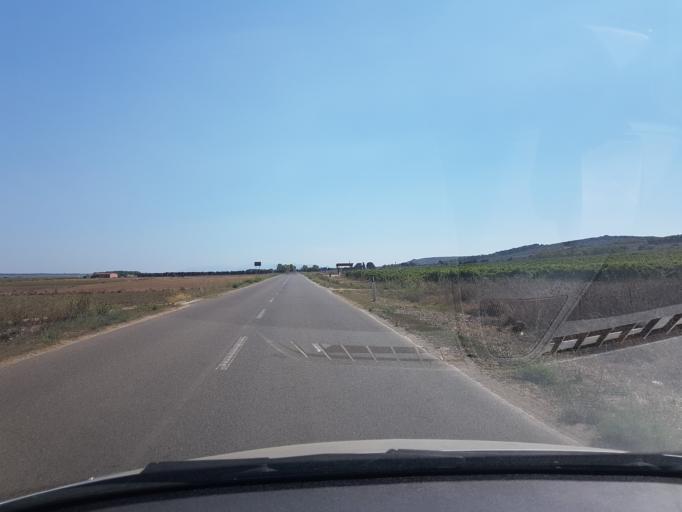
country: IT
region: Sardinia
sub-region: Provincia di Oristano
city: Nurachi
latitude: 39.9651
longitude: 8.4533
